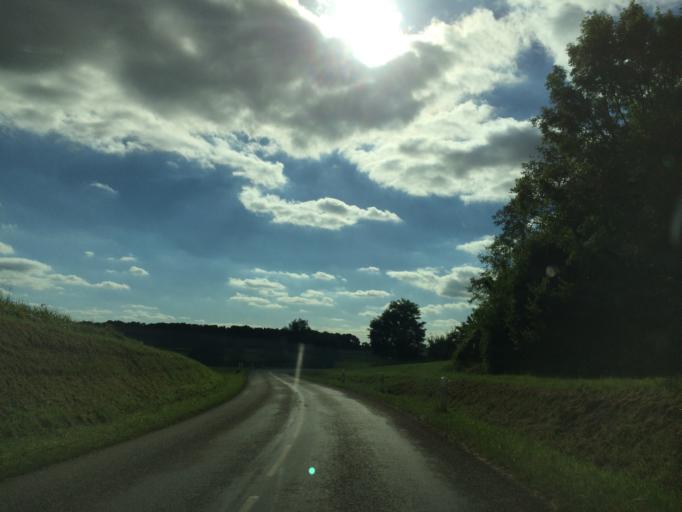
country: FR
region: Alsace
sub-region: Departement du Bas-Rhin
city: Betschdorf
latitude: 48.8977
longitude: 7.9459
